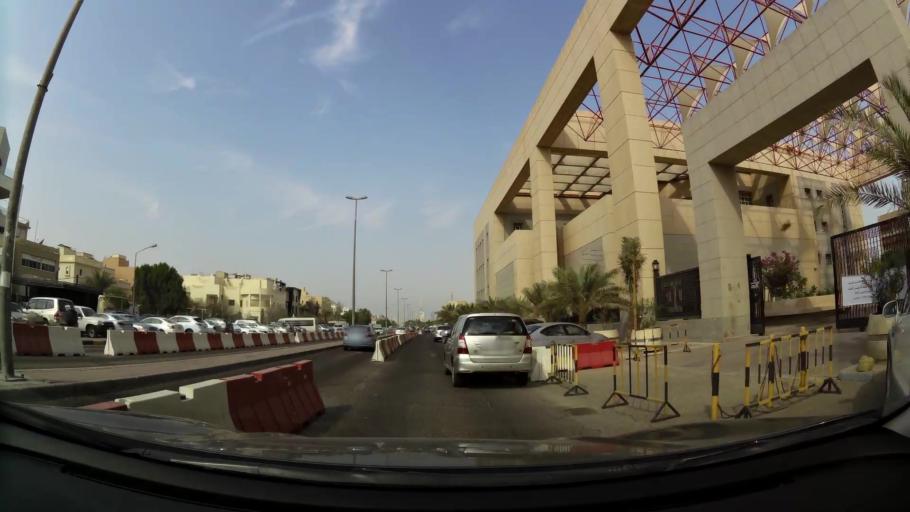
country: KW
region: Al Asimah
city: Ash Shamiyah
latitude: 29.3212
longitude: 47.9699
